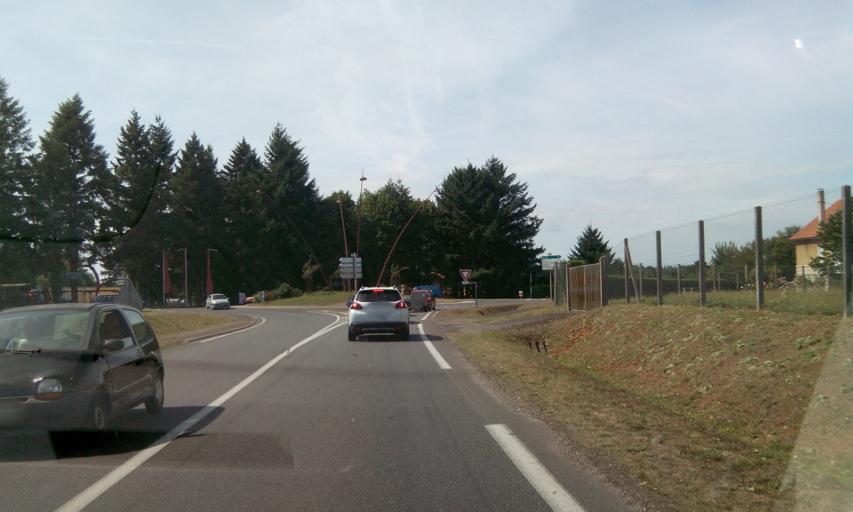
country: FR
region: Poitou-Charentes
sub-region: Departement de la Vienne
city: Civray
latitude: 46.1505
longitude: 0.2778
